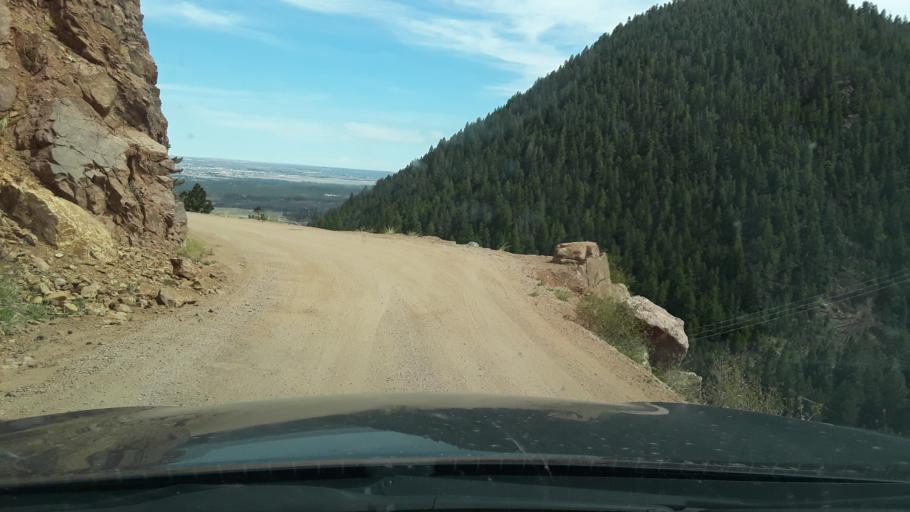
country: US
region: Colorado
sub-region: El Paso County
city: Palmer Lake
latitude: 39.0678
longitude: -104.9273
